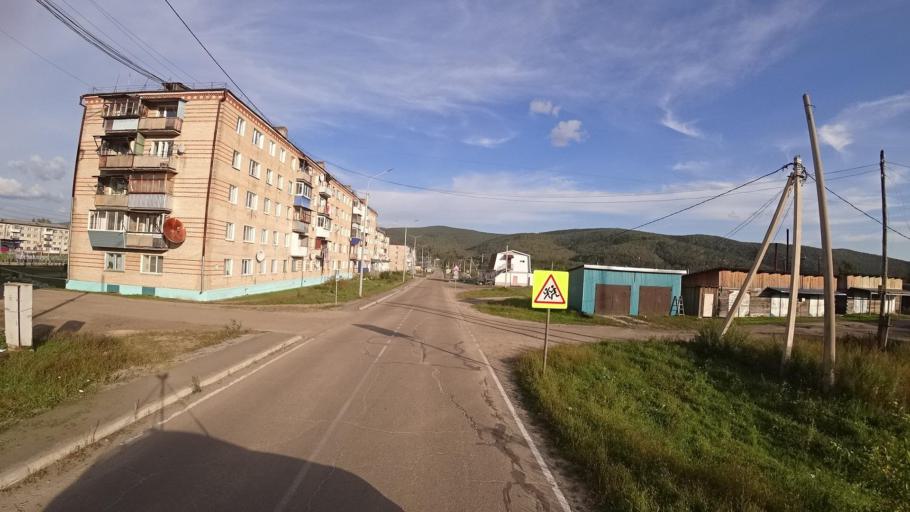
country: RU
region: Jewish Autonomous Oblast
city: Kul'dur
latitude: 49.2024
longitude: 131.6231
